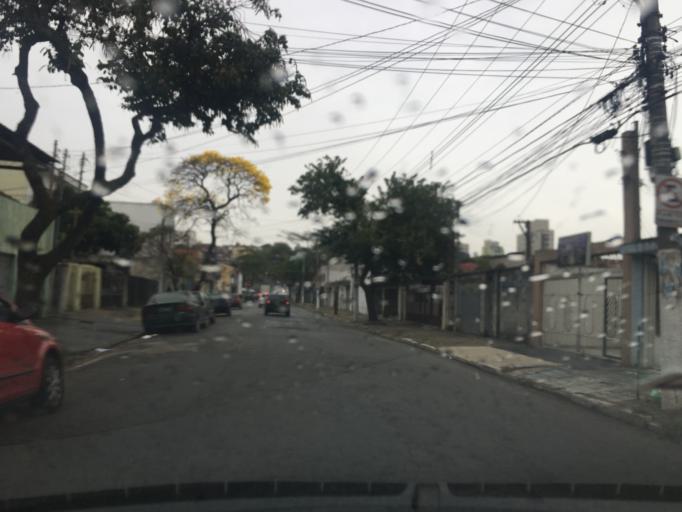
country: BR
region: Sao Paulo
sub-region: Guarulhos
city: Guarulhos
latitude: -23.5189
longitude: -46.5498
